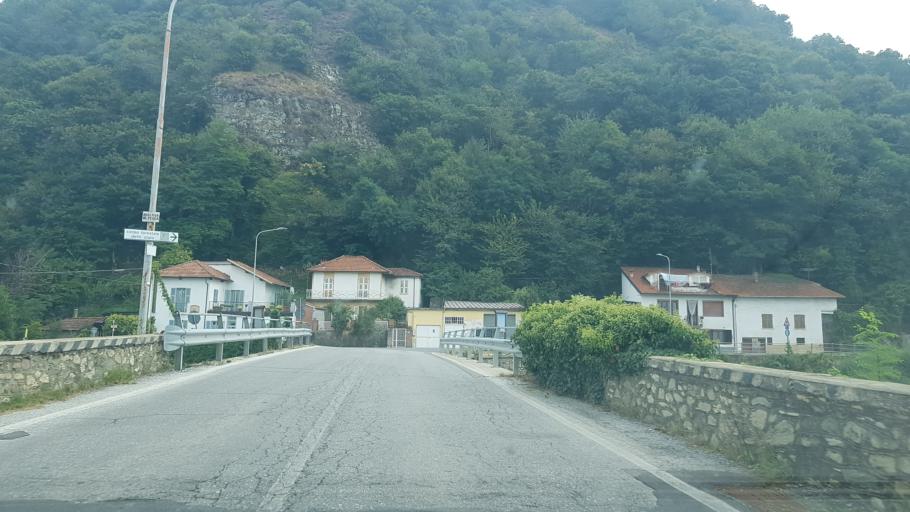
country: IT
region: Piedmont
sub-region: Provincia di Cuneo
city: Chiusa di Pesio
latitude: 44.3268
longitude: 7.6796
